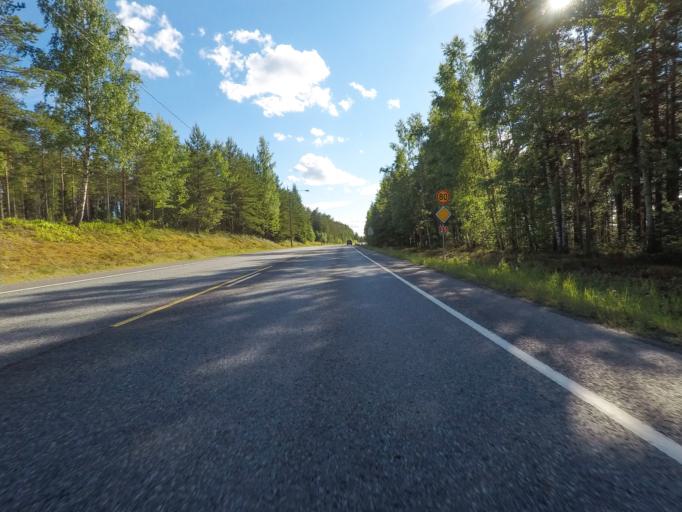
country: FI
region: Uusimaa
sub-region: Helsinki
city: Vihti
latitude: 60.3408
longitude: 24.3030
